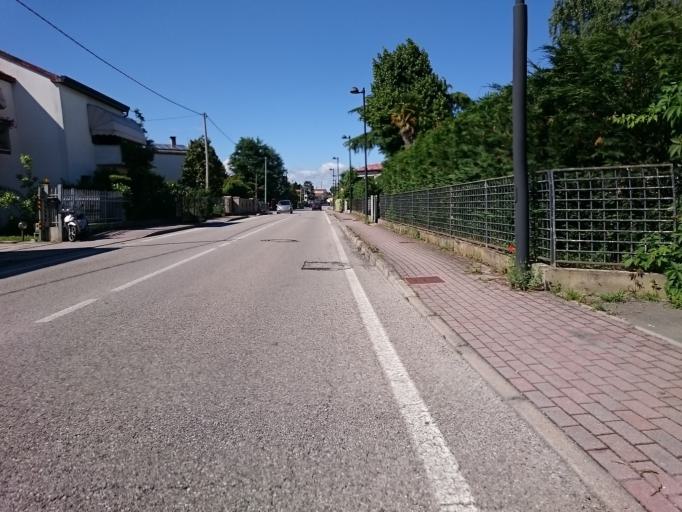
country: IT
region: Veneto
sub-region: Provincia di Venezia
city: Campolongo Maggiore Liettoli
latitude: 45.3374
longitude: 12.0214
